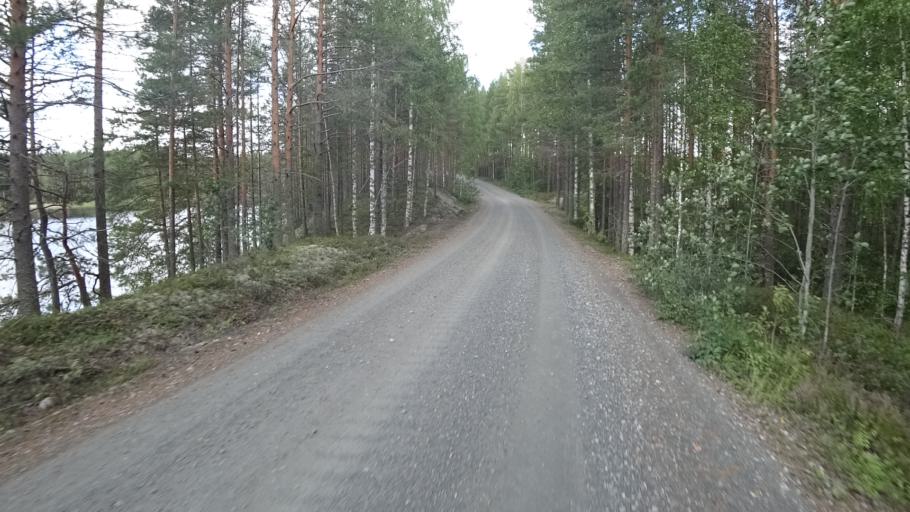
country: FI
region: North Karelia
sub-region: Joensuu
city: Ilomantsi
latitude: 62.6177
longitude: 31.1961
